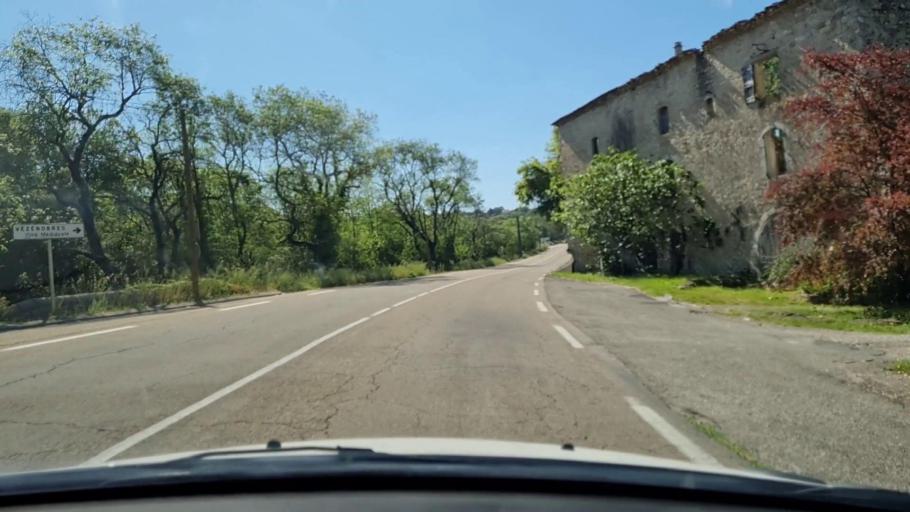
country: FR
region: Languedoc-Roussillon
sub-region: Departement du Gard
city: Vezenobres
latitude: 44.0621
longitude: 4.1263
